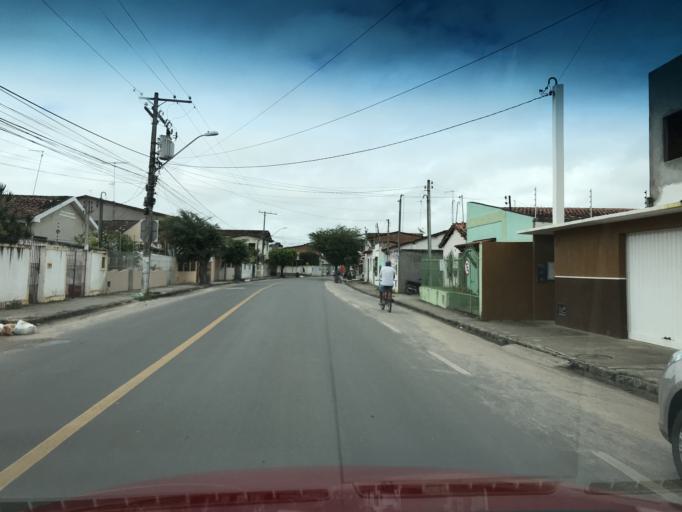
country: BR
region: Bahia
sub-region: Cruz Das Almas
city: Cruz das Almas
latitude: -12.6653
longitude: -39.1000
